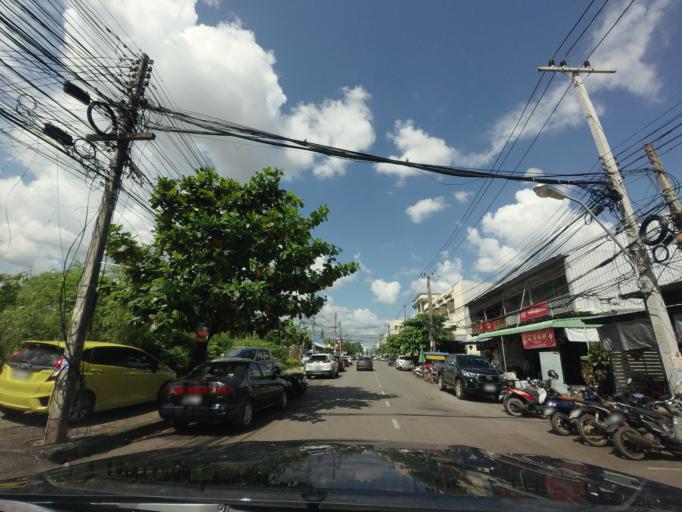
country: TH
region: Changwat Udon Thani
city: Udon Thani
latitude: 17.4022
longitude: 102.7850
